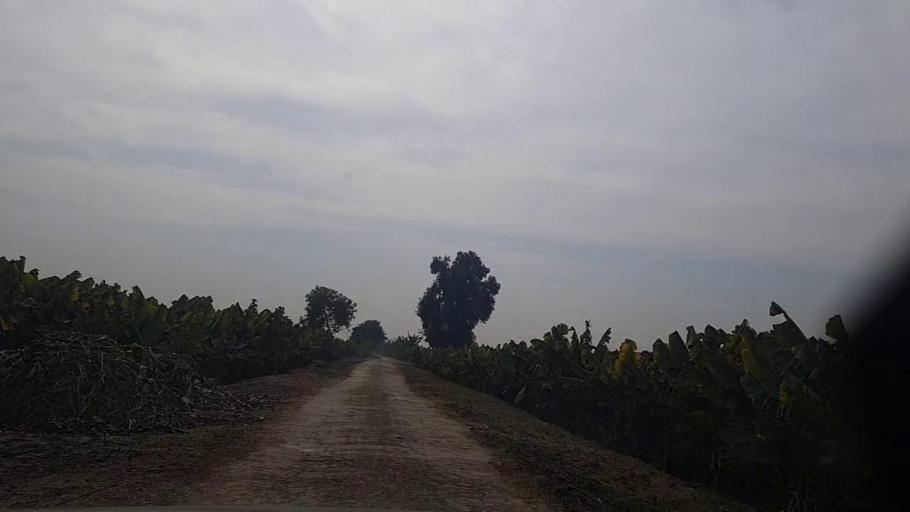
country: PK
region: Sindh
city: Sakrand
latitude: 26.2384
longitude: 68.2972
